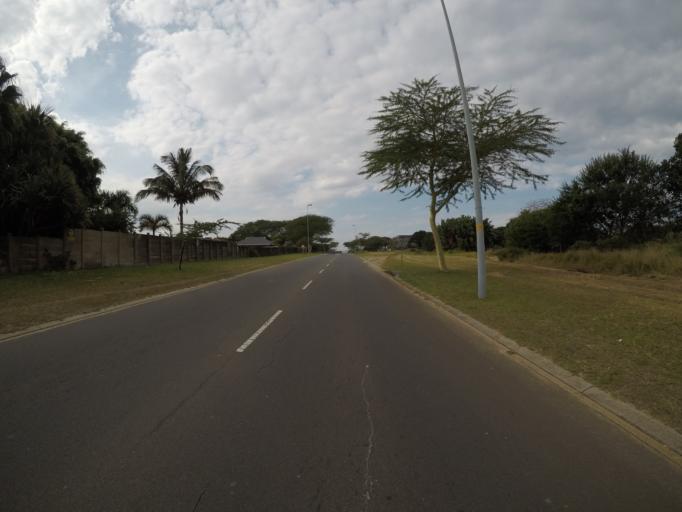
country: ZA
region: KwaZulu-Natal
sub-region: uThungulu District Municipality
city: Richards Bay
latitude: -28.7382
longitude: 32.0798
